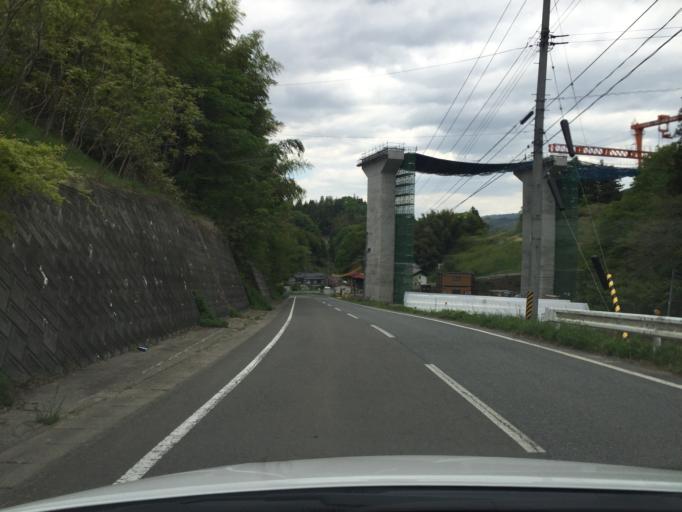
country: JP
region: Fukushima
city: Yanagawamachi-saiwaicho
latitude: 37.7461
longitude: 140.6393
